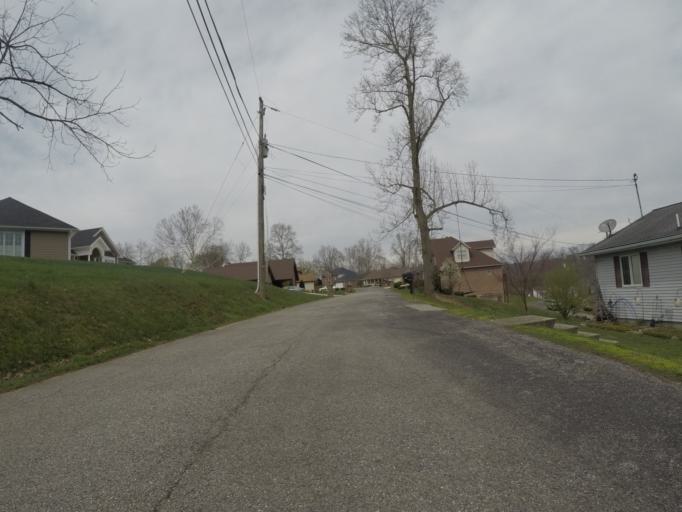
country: US
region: West Virginia
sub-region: Cabell County
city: Pea Ridge
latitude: 38.4125
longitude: -82.3249
